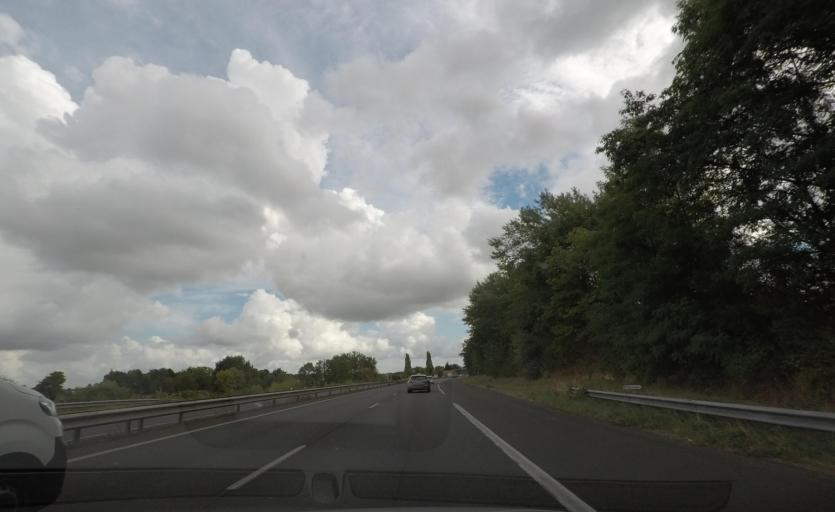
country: FR
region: Pays de la Loire
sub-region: Departement de Maine-et-Loire
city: Pellouailles-les-Vignes
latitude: 47.5148
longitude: -0.4397
